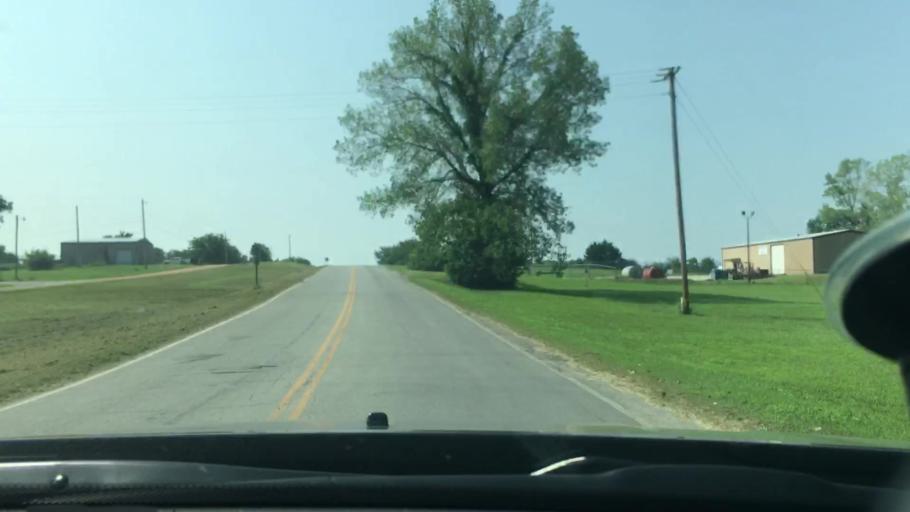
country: US
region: Oklahoma
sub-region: Pontotoc County
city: Ada
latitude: 34.6525
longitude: -96.5302
